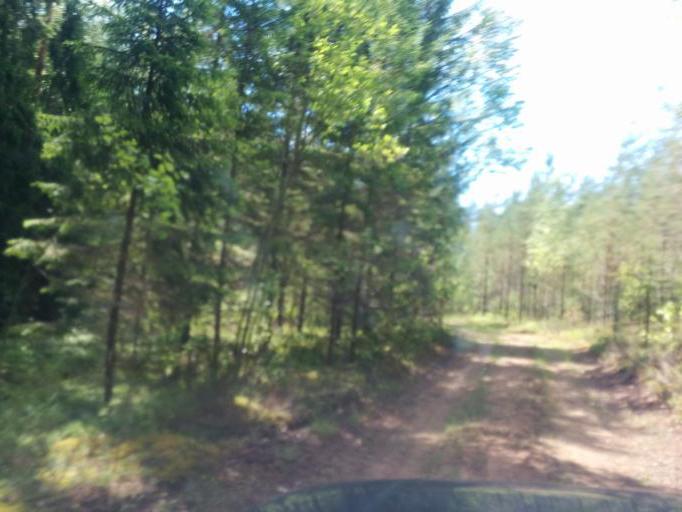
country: LV
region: Vilaka
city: Vilaka
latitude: 57.3341
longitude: 27.6926
